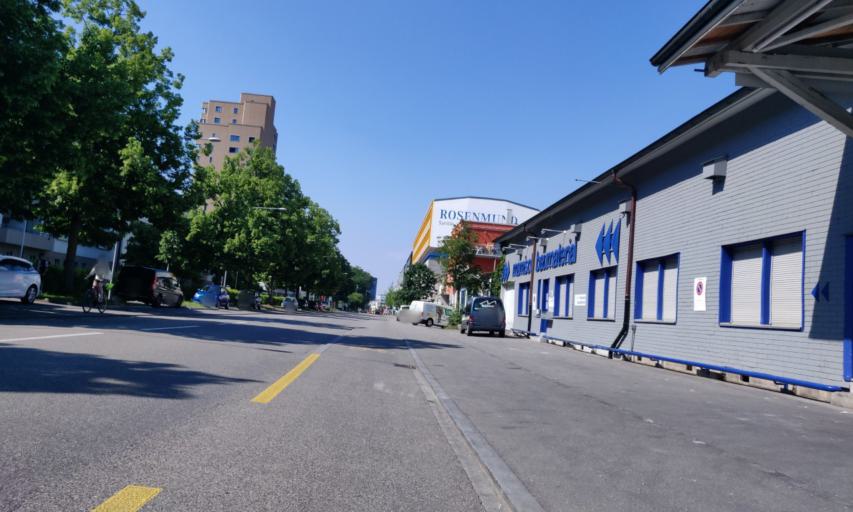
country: CH
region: Basel-Landschaft
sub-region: Bezirk Arlesheim
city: Munchenstein
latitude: 47.5320
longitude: 7.6053
